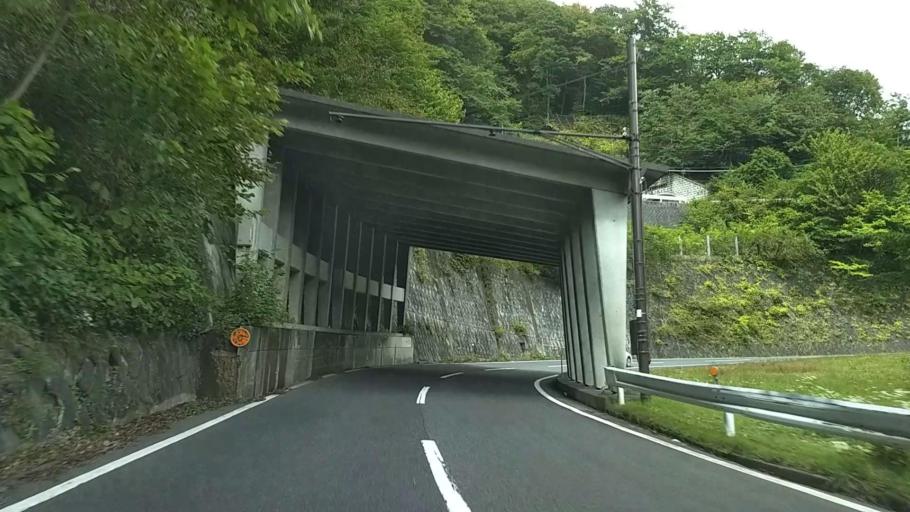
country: JP
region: Tochigi
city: Nikko
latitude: 36.7348
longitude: 139.5146
